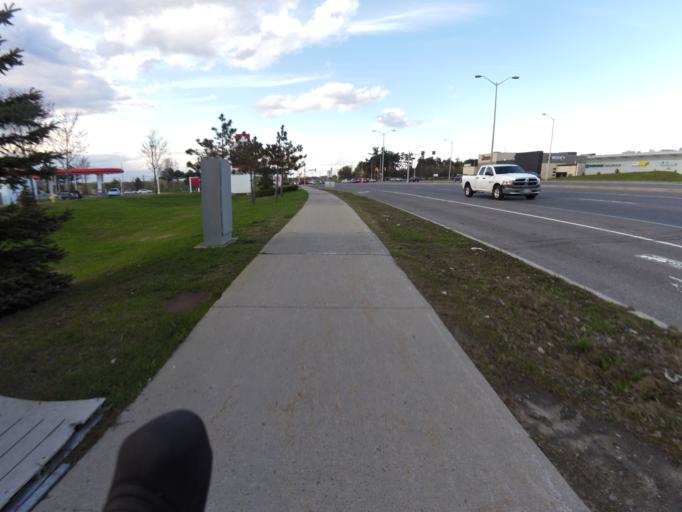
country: CA
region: Ontario
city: Ottawa
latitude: 45.3331
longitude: -75.6935
